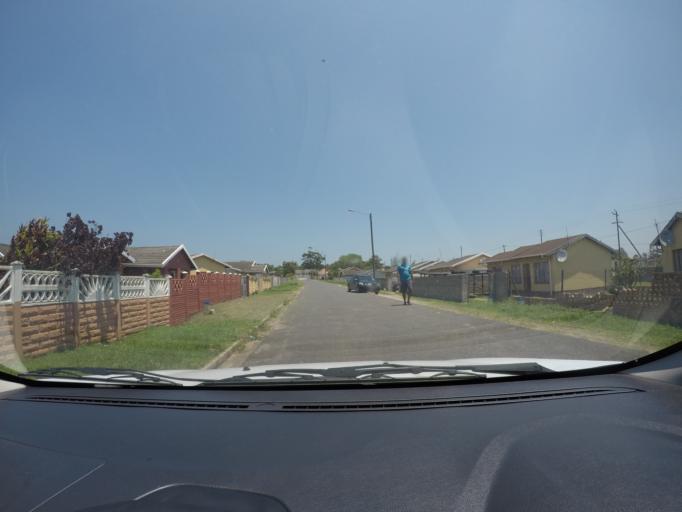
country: ZA
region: KwaZulu-Natal
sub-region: uThungulu District Municipality
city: eSikhawini
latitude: -28.8907
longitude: 31.8815
